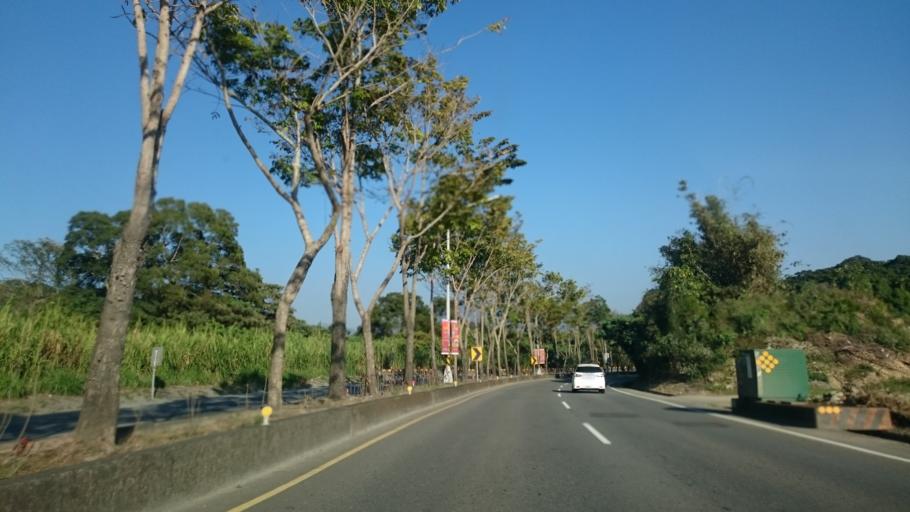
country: TW
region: Taiwan
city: Lugu
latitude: 23.8329
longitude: 120.7434
